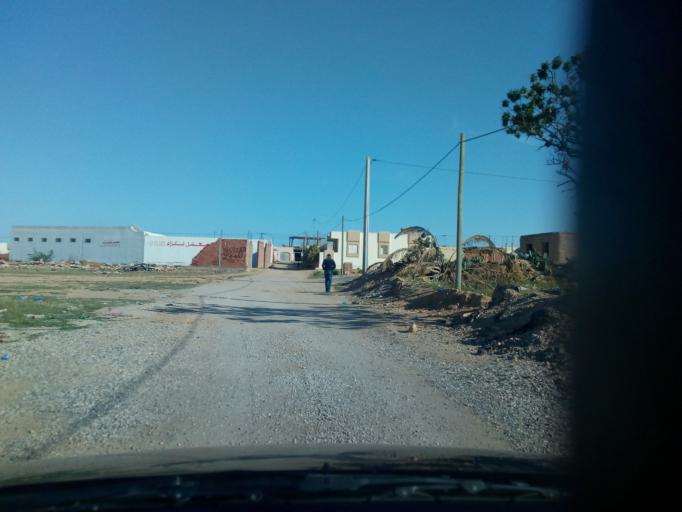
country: TN
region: Safaqis
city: Sfax
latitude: 34.7286
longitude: 10.6248
